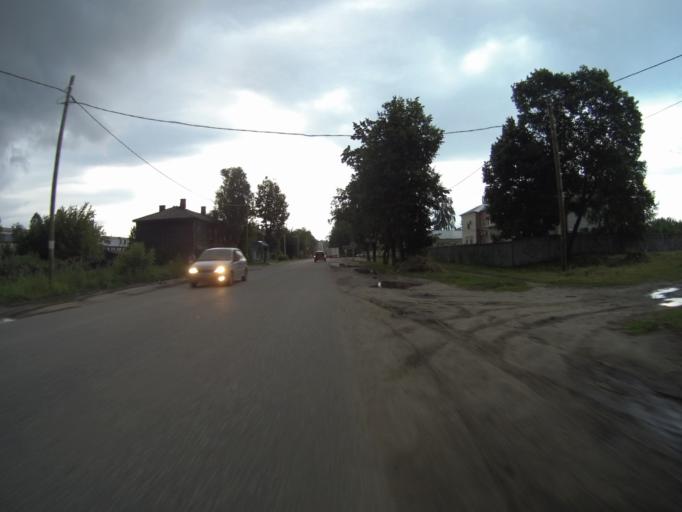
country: RU
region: Vladimir
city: Kameshkovo
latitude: 56.3474
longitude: 40.9871
